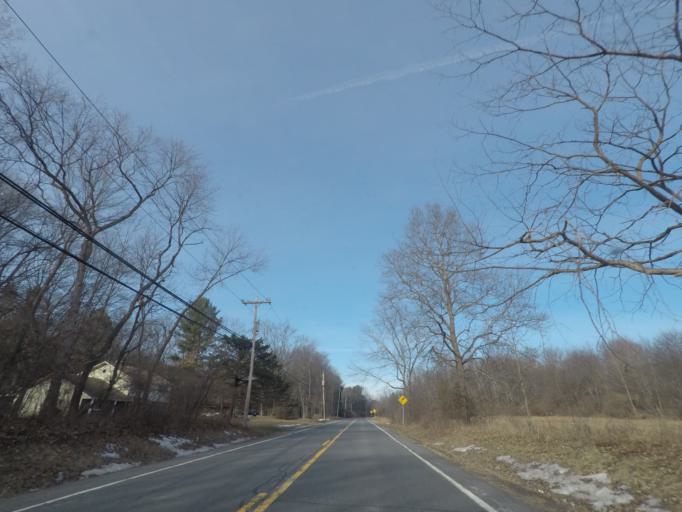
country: US
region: New York
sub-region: Rensselaer County
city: Nassau
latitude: 42.4904
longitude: -73.6248
